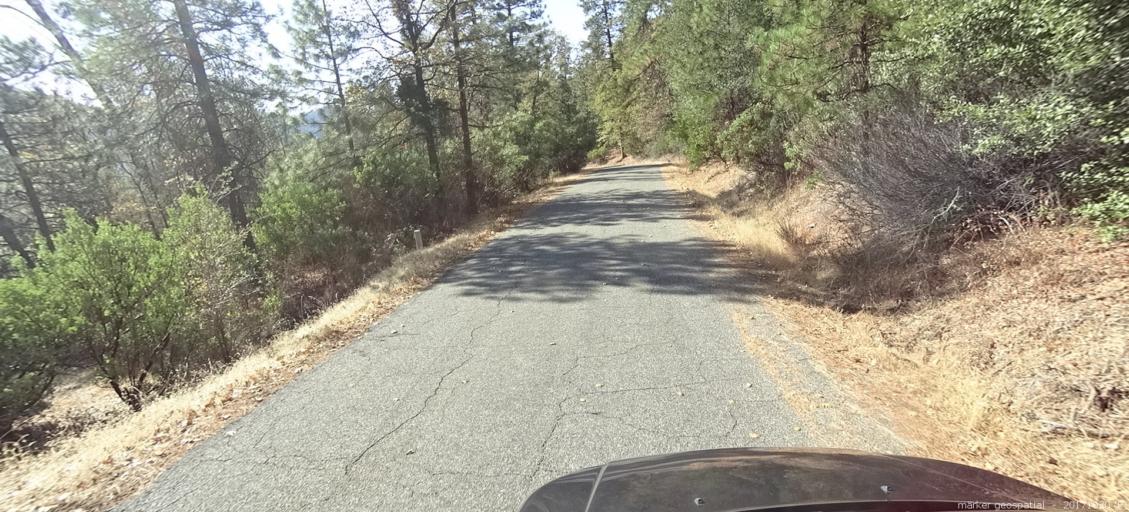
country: US
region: California
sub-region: Shasta County
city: Shingletown
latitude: 40.5762
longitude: -121.8750
